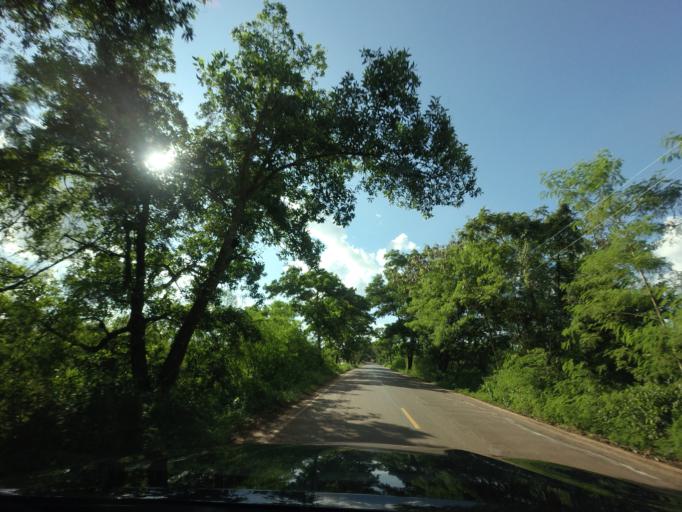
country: TH
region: Changwat Udon Thani
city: Ban Dung
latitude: 17.7429
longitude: 103.3396
